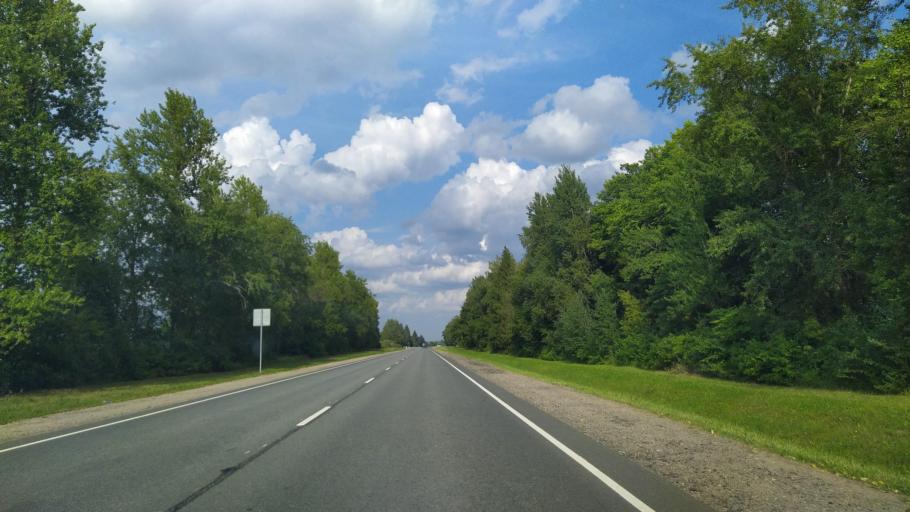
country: RU
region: Novgorod
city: Shimsk
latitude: 58.1884
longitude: 30.5586
